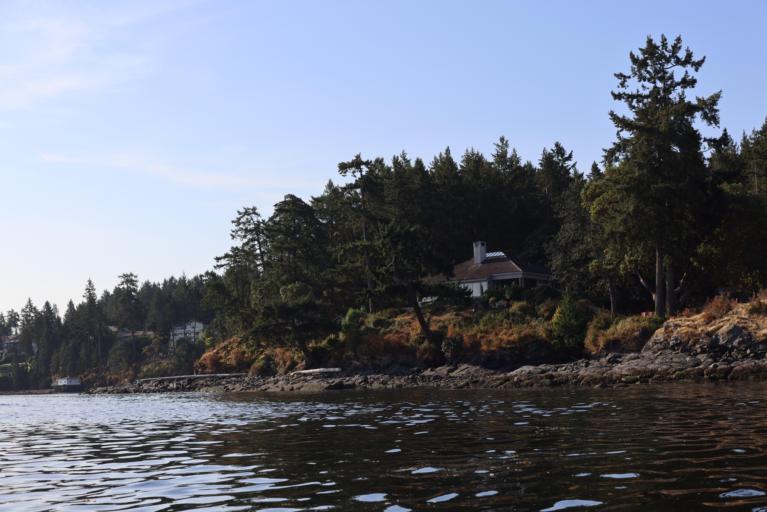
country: CA
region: British Columbia
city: North Saanich
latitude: 48.6935
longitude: -123.4222
